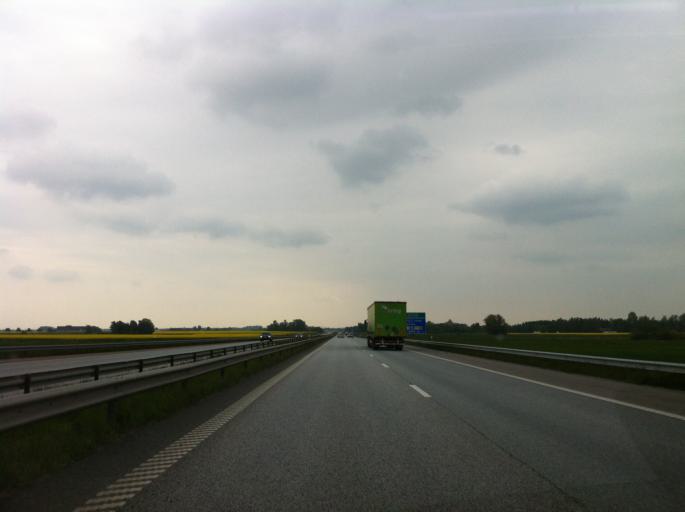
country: SE
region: Skane
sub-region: Lomma Kommun
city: Lomma
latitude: 55.7003
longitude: 13.0977
